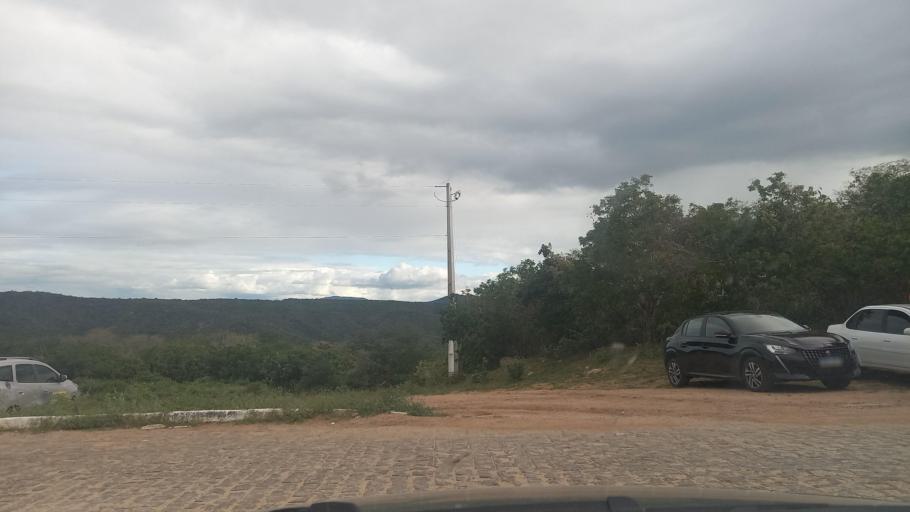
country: BR
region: Sergipe
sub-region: Caninde De Sao Francisco
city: Caninde de Sao Francisco
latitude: -9.6180
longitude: -37.8117
